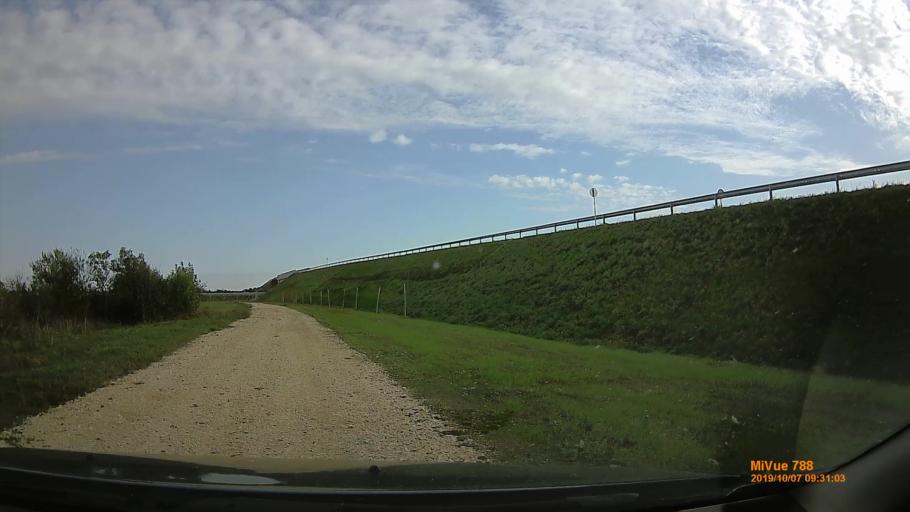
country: HU
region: Bekes
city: Szarvas
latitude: 46.8121
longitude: 20.6475
